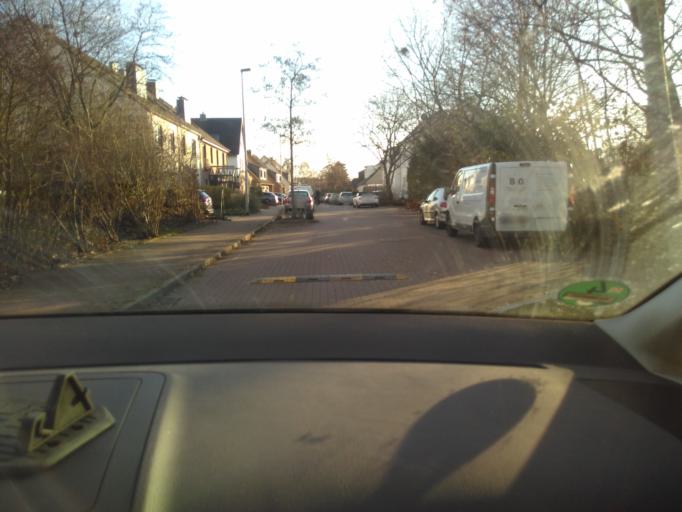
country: DE
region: North Rhine-Westphalia
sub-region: Regierungsbezirk Dusseldorf
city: Hilden
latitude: 51.1639
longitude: 6.9539
